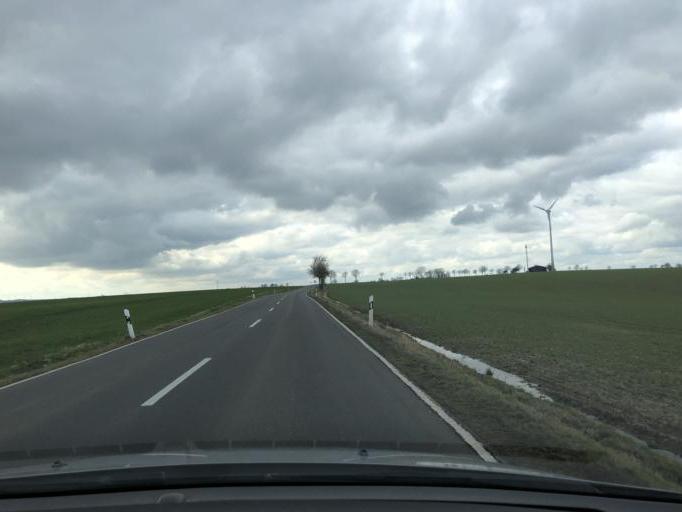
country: DE
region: Saxony
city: Grossweitzschen
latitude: 51.1518
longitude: 13.0810
